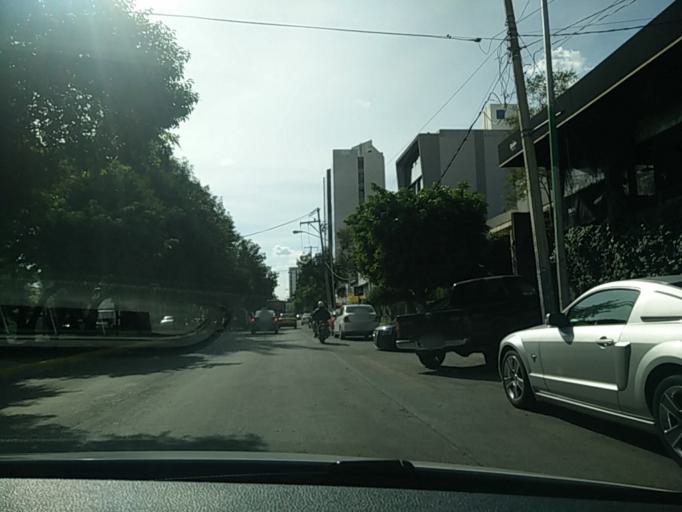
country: MX
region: Jalisco
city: Guadalajara
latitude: 20.6797
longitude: -103.3854
